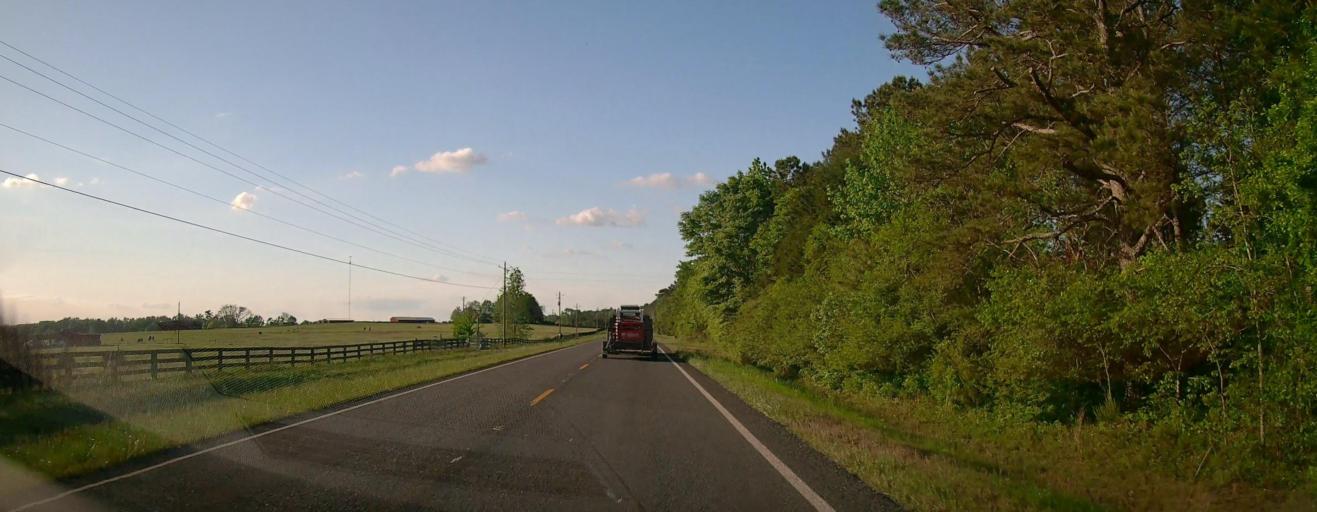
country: US
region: Georgia
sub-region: Jasper County
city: Monticello
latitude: 33.4325
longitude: -83.6194
